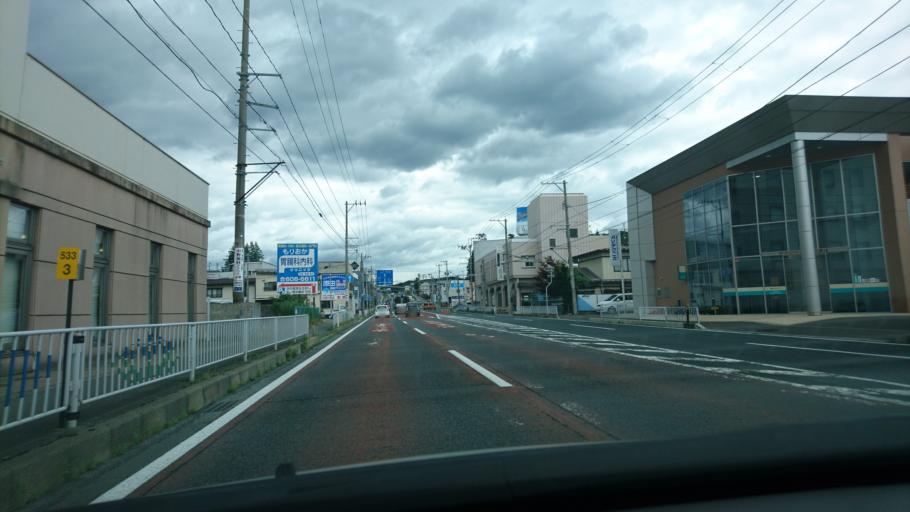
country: JP
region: Iwate
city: Morioka-shi
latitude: 39.6940
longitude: 141.1668
